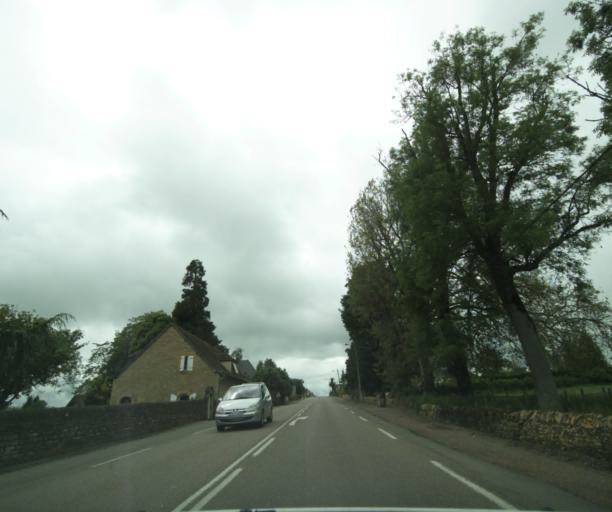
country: FR
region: Bourgogne
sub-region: Departement de Saone-et-Loire
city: Charolles
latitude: 46.4371
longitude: 4.2670
